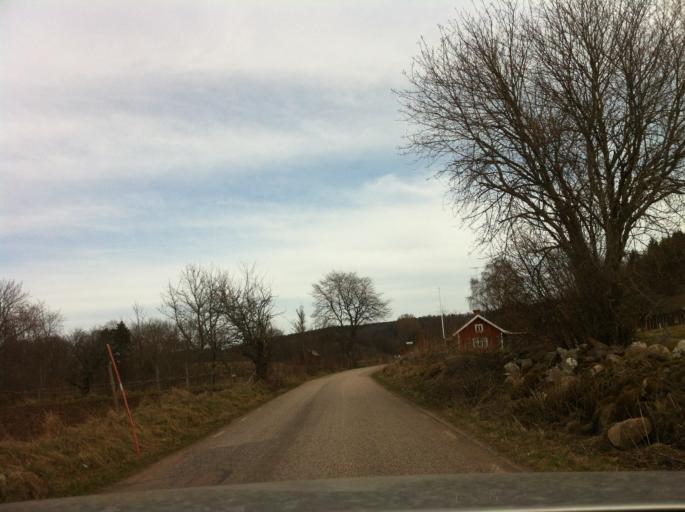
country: SE
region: Vaestra Goetaland
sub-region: Skovde Kommun
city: Skoevde
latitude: 58.4490
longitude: 13.7109
